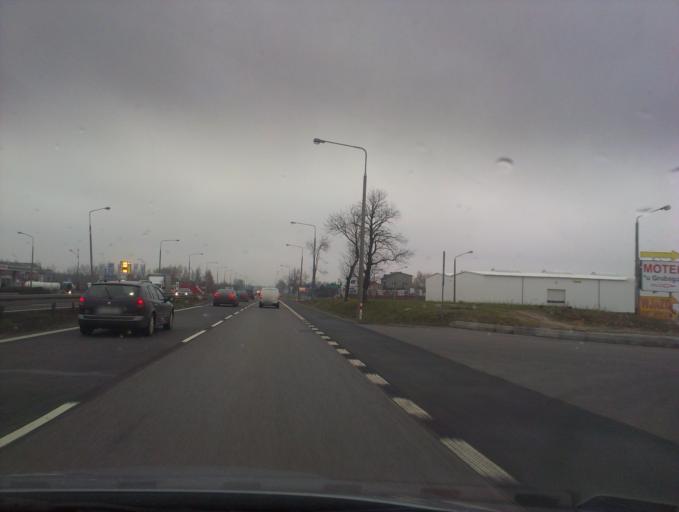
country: PL
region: Masovian Voivodeship
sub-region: Powiat radomski
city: Jedlinsk
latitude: 51.4750
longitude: 21.1321
